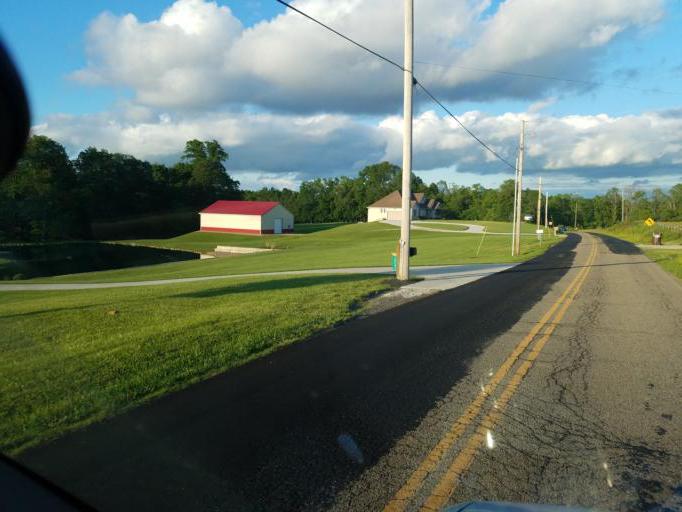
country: US
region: Ohio
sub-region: Knox County
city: Mount Vernon
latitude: 40.3812
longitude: -82.5601
